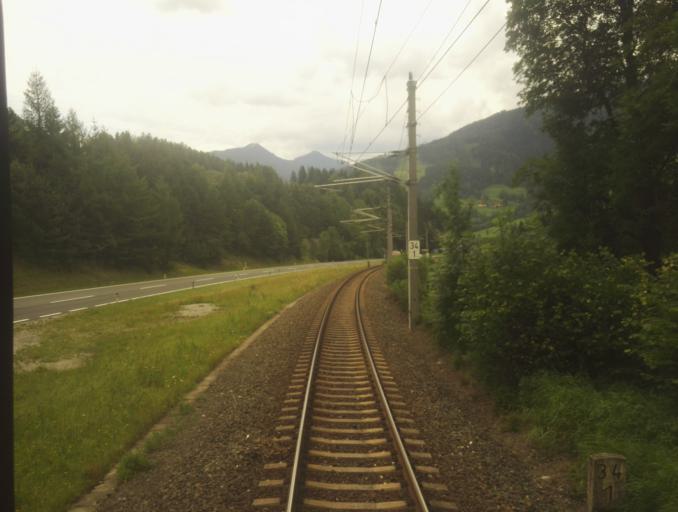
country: AT
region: Salzburg
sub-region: Politischer Bezirk Sankt Johann im Pongau
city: Forstau
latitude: 47.3975
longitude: 13.5903
